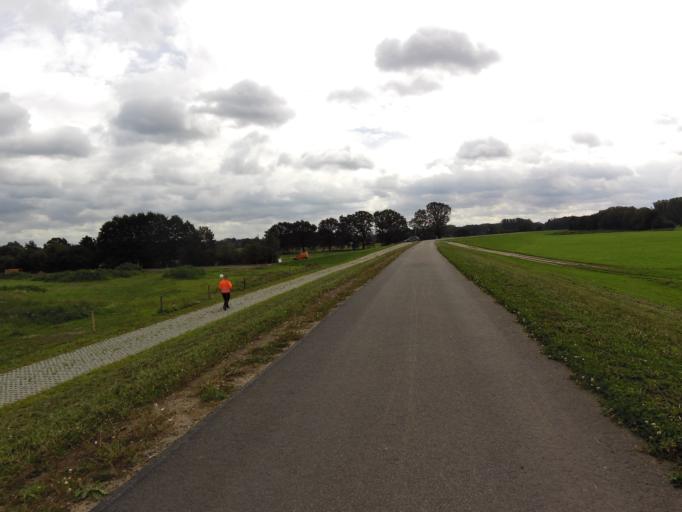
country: DE
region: Saxony-Anhalt
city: Havelberg
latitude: 52.8451
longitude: 12.0444
